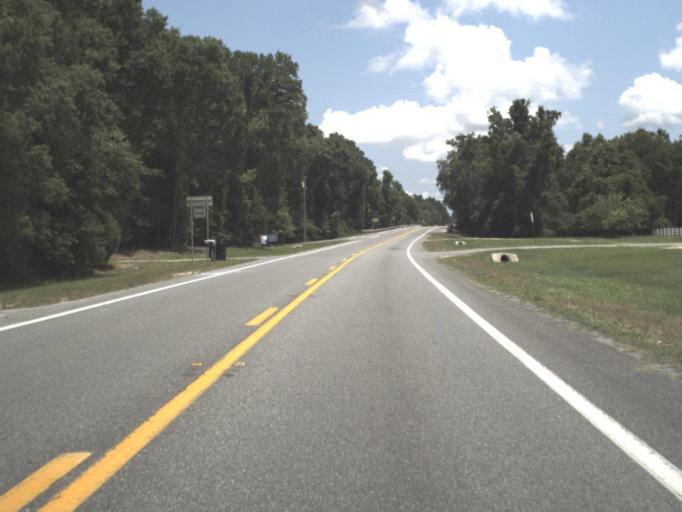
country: US
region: Florida
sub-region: Alachua County
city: High Springs
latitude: 29.8498
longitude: -82.6083
